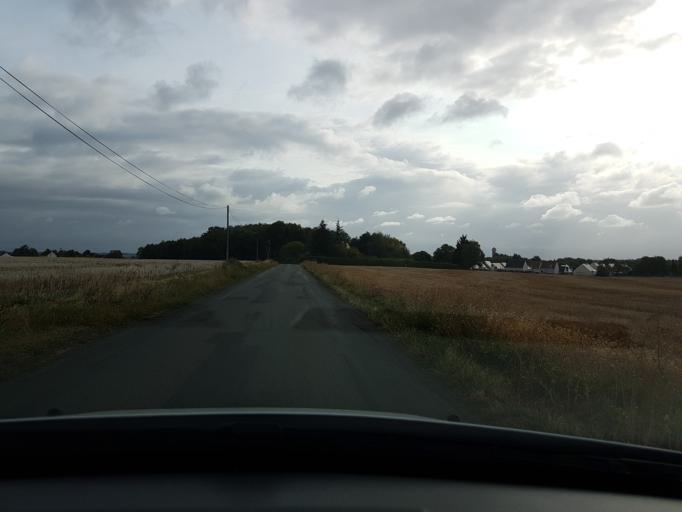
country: FR
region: Centre
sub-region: Departement d'Indre-et-Loire
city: Azay-sur-Cher
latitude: 47.3392
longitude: 0.8286
